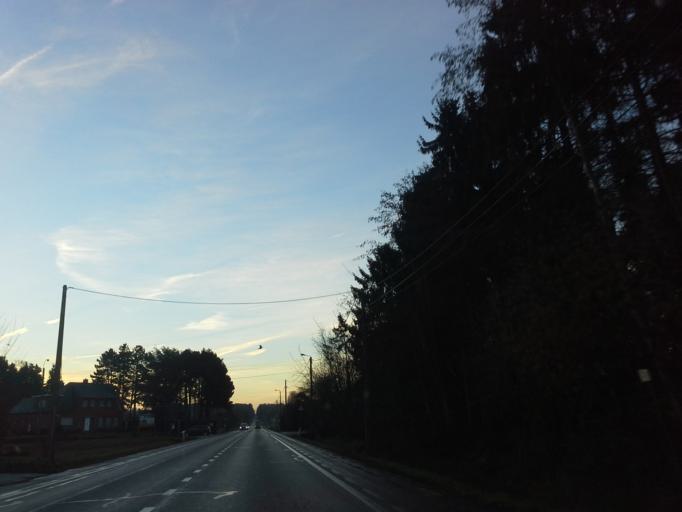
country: BE
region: Flanders
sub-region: Provincie Antwerpen
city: Laakdal
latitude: 51.0666
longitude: 5.0396
